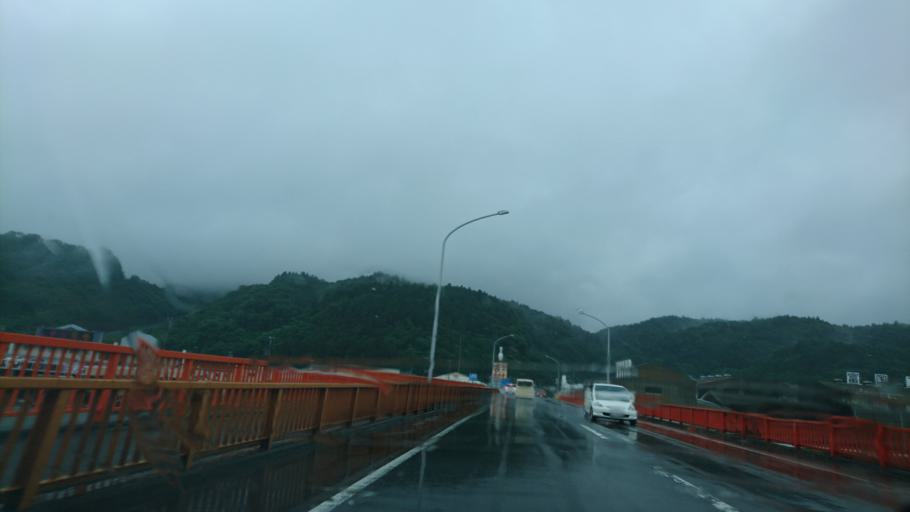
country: JP
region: Miyagi
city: Ishinomaki
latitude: 38.4378
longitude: 141.3170
